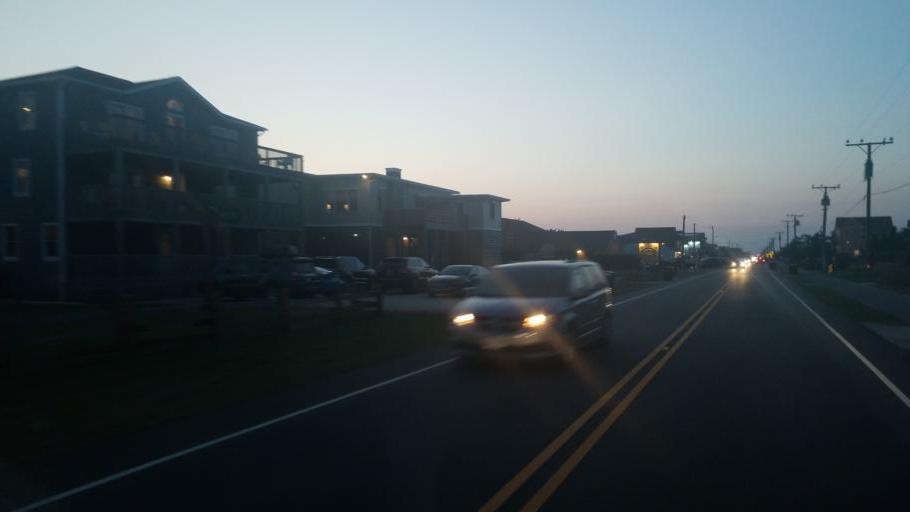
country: US
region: North Carolina
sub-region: Dare County
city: Nags Head
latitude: 35.9876
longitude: -75.6415
